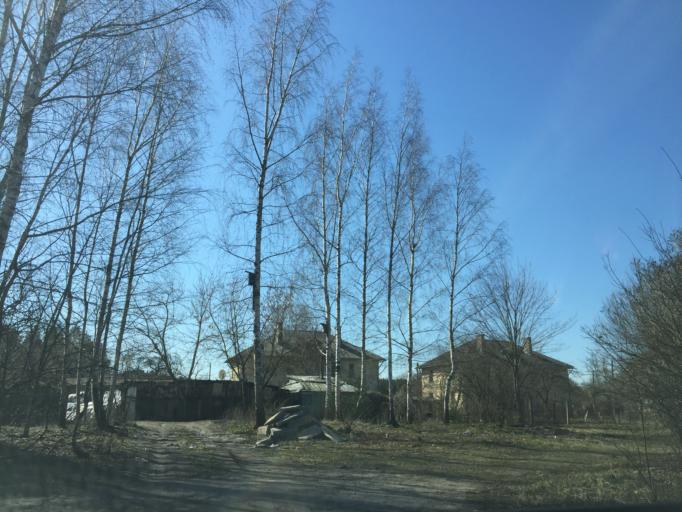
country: LV
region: Stopini
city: Ulbroka
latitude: 56.9368
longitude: 24.2271
